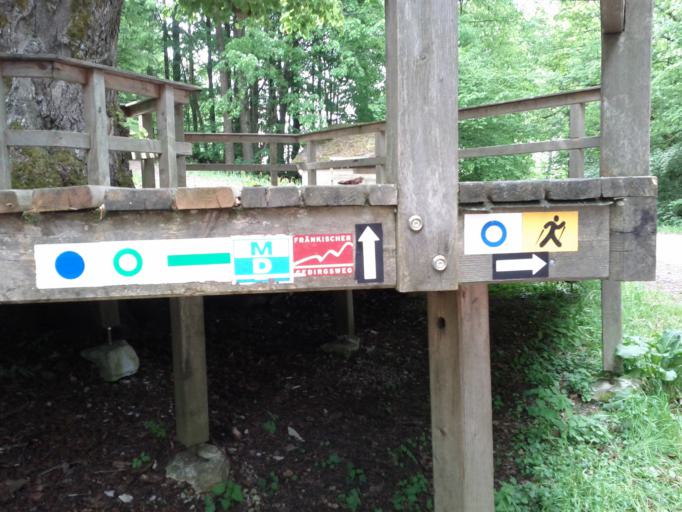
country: DE
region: Bavaria
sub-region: Regierungsbezirk Mittelfranken
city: Simmelsdorf
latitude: 49.6353
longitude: 11.4067
